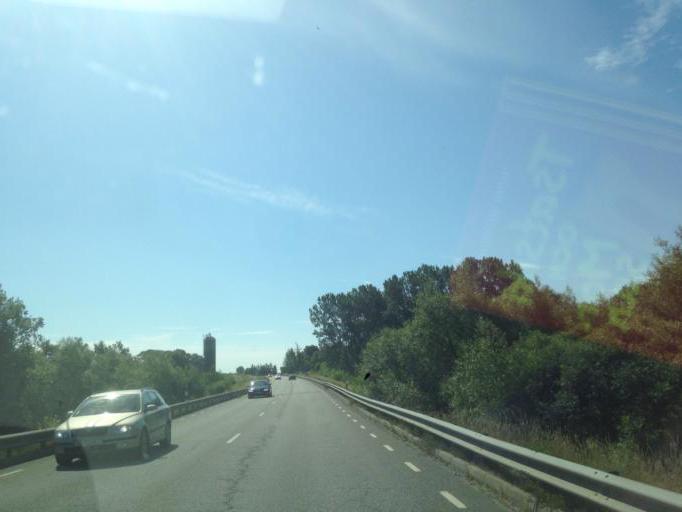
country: SE
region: Skane
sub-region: Simrishamns Kommun
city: Kivik
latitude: 55.6279
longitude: 14.2562
